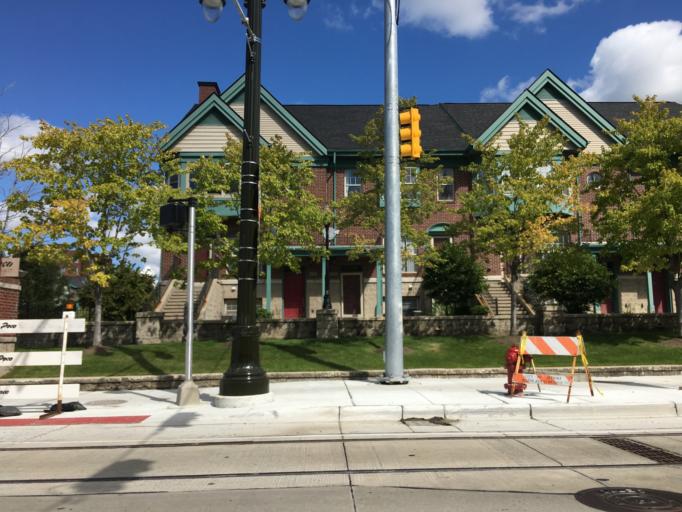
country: US
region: Michigan
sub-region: Wayne County
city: Detroit
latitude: 42.3416
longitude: -83.0539
